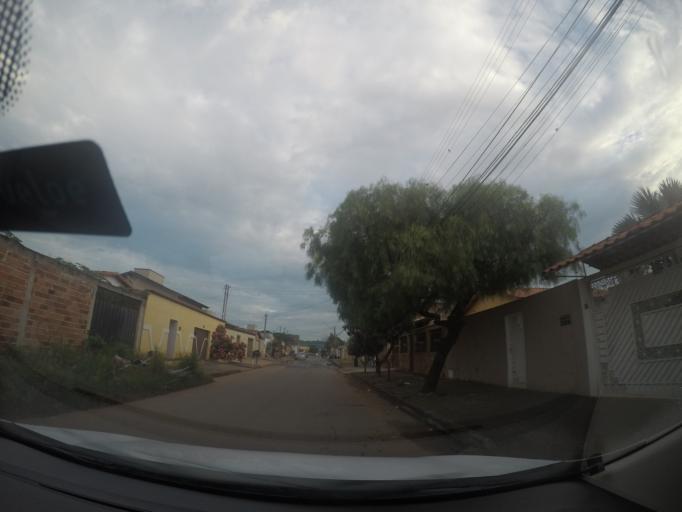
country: BR
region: Goias
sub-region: Goiania
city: Goiania
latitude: -16.6878
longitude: -49.3457
